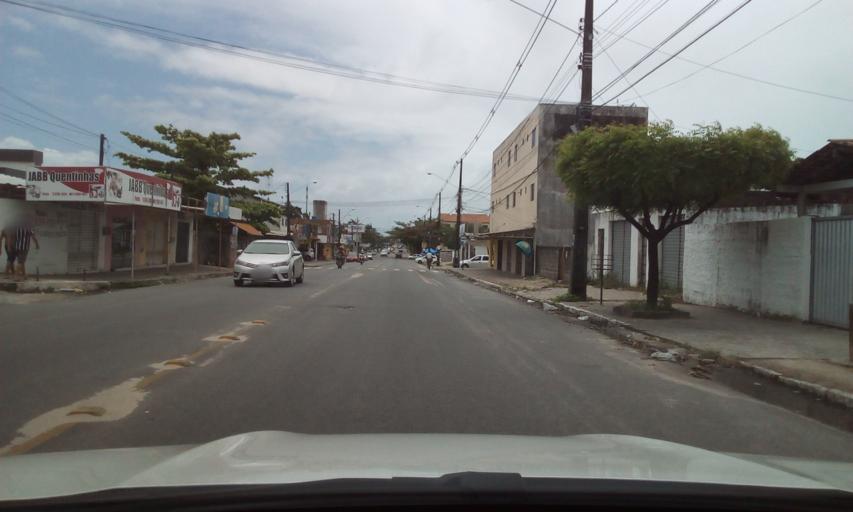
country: BR
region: Paraiba
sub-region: Joao Pessoa
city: Joao Pessoa
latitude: -7.1784
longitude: -34.8369
